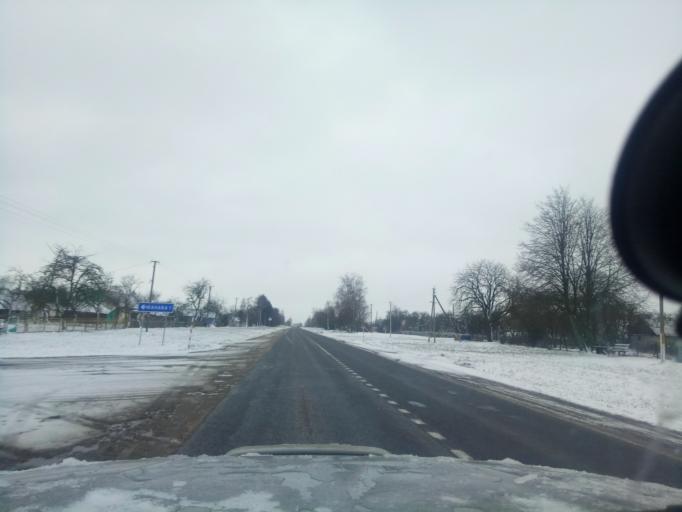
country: BY
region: Minsk
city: Klyetsk
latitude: 53.1231
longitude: 26.6672
